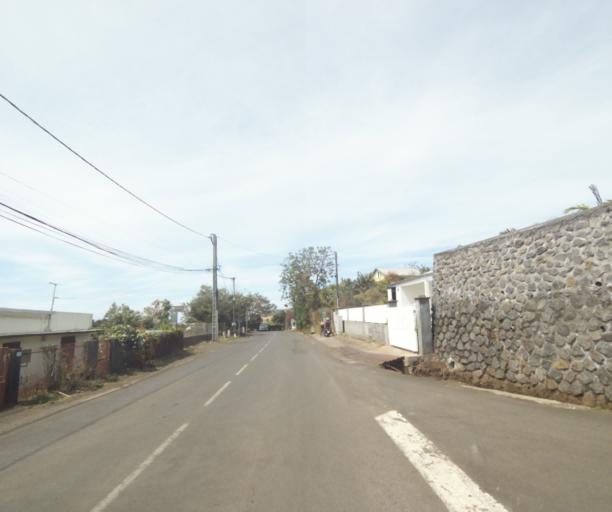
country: RE
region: Reunion
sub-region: Reunion
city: Saint-Paul
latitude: -21.0515
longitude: 55.2805
